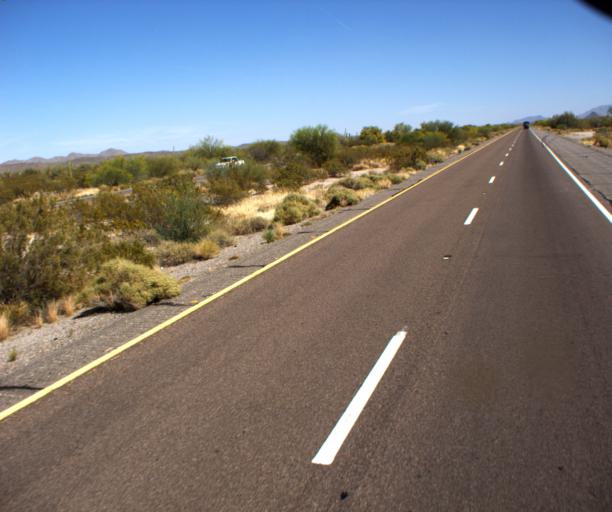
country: US
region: Arizona
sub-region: Maricopa County
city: Gila Bend
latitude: 32.8576
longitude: -112.3850
